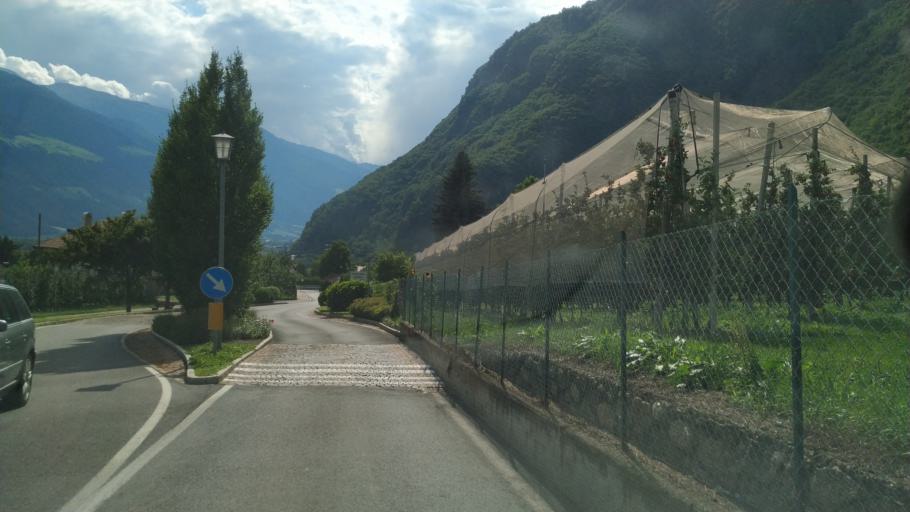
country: IT
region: Trentino-Alto Adige
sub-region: Bolzano
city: Rabla
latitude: 46.6759
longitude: 11.0609
